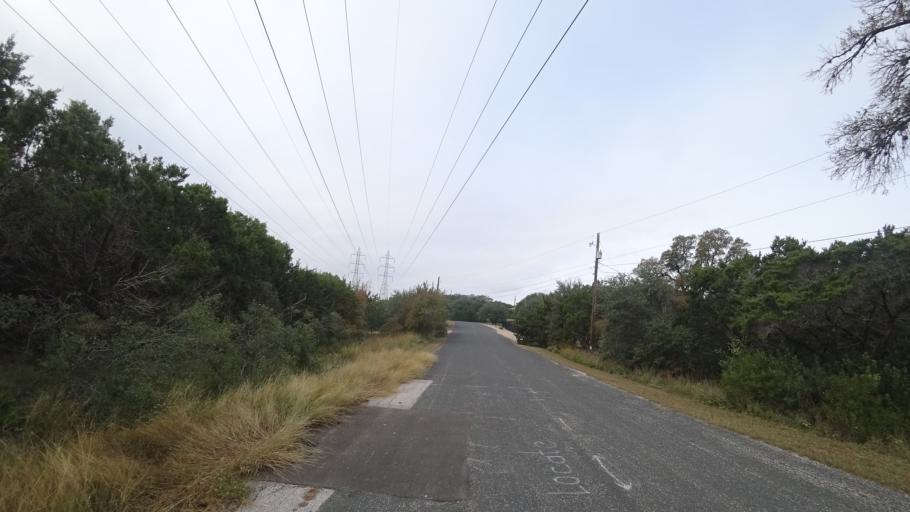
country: US
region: Texas
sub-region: Travis County
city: Hudson Bend
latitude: 30.3923
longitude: -97.9139
